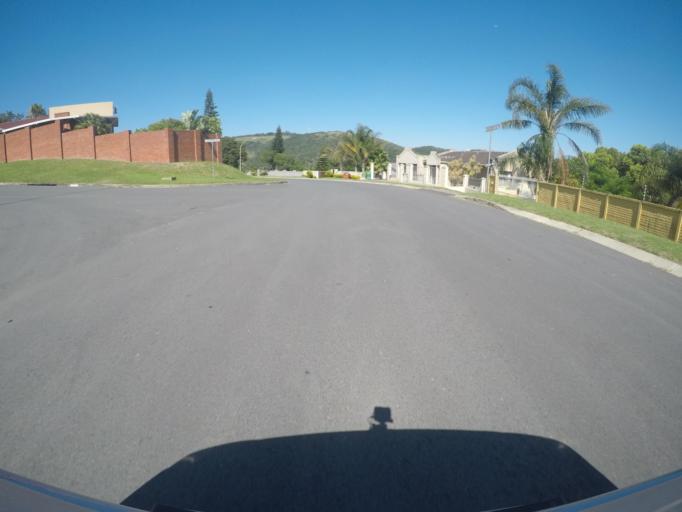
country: ZA
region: Eastern Cape
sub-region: Buffalo City Metropolitan Municipality
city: East London
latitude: -32.9546
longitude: 27.9106
